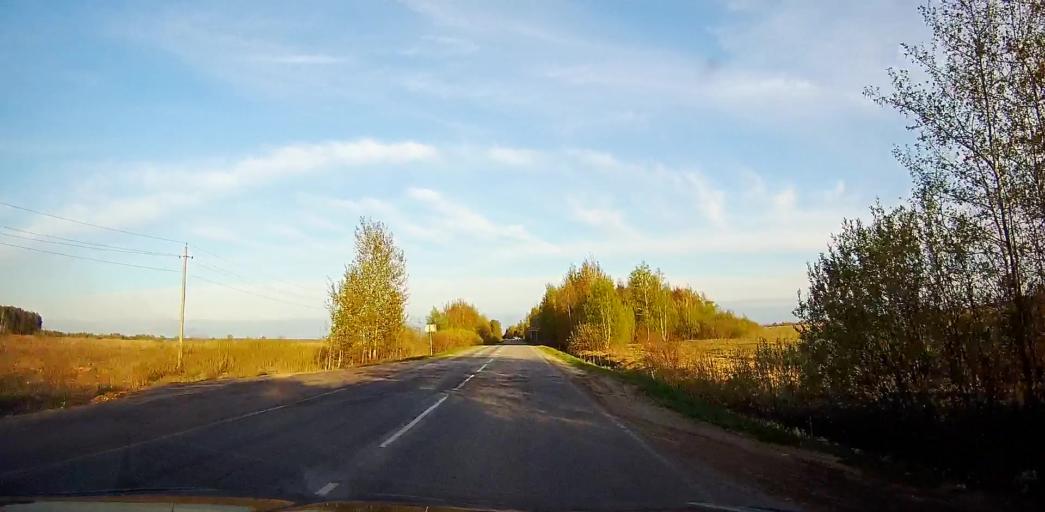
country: RU
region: Moskovskaya
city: Bronnitsy
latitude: 55.2777
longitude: 38.2209
